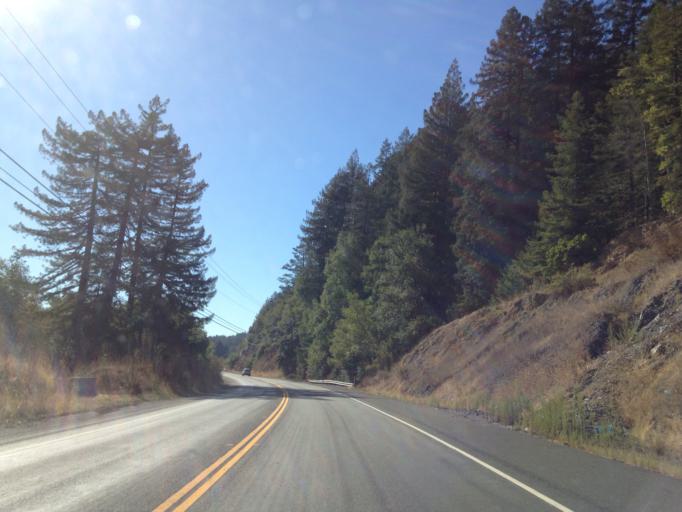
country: US
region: California
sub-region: Sonoma County
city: Guerneville
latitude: 38.5070
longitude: -122.9466
